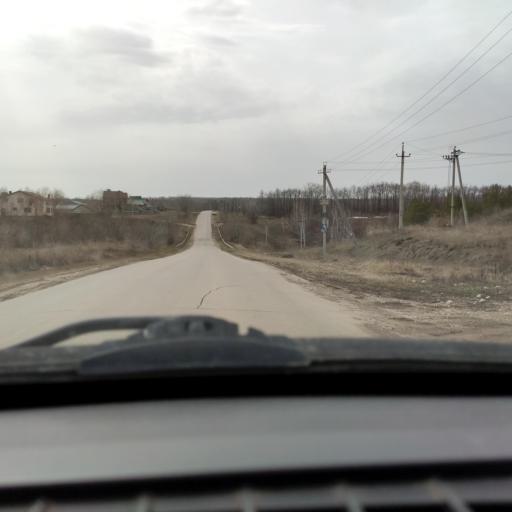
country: RU
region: Samara
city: Dubovyy Umet
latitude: 53.0428
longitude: 50.1788
